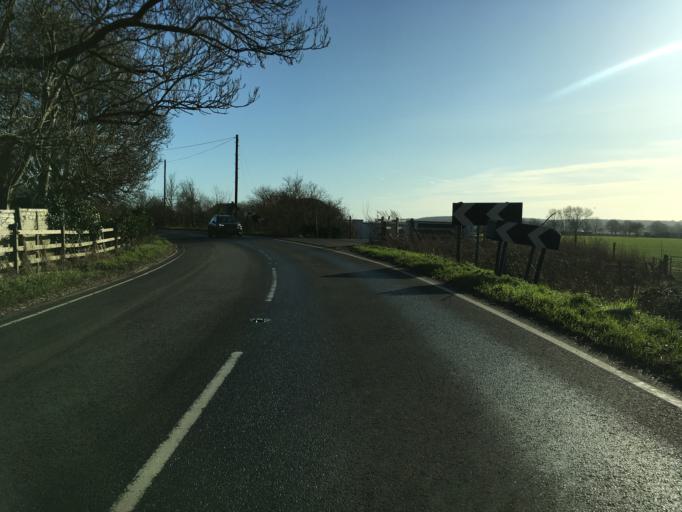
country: GB
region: England
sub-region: Warwickshire
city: Wellesbourne Mountford
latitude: 52.1992
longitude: -1.6213
